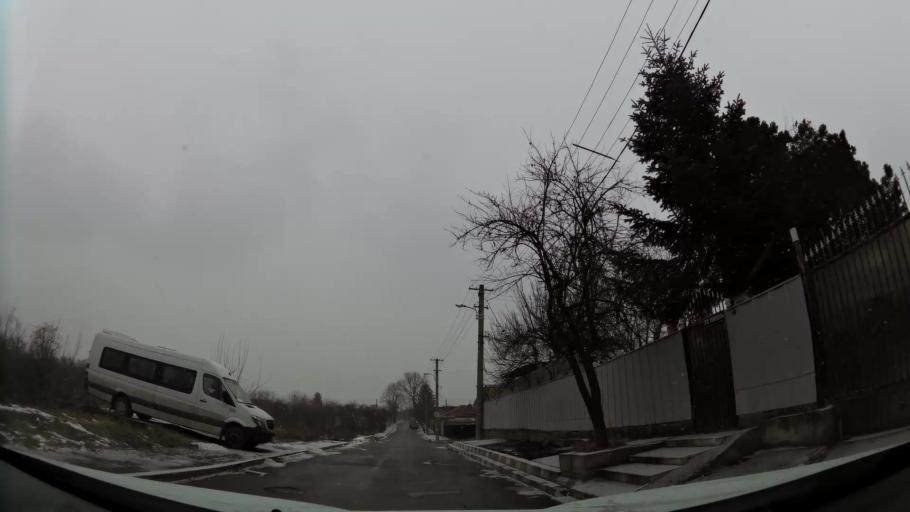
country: RO
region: Prahova
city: Ploiesti
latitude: 44.9515
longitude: 26.0377
